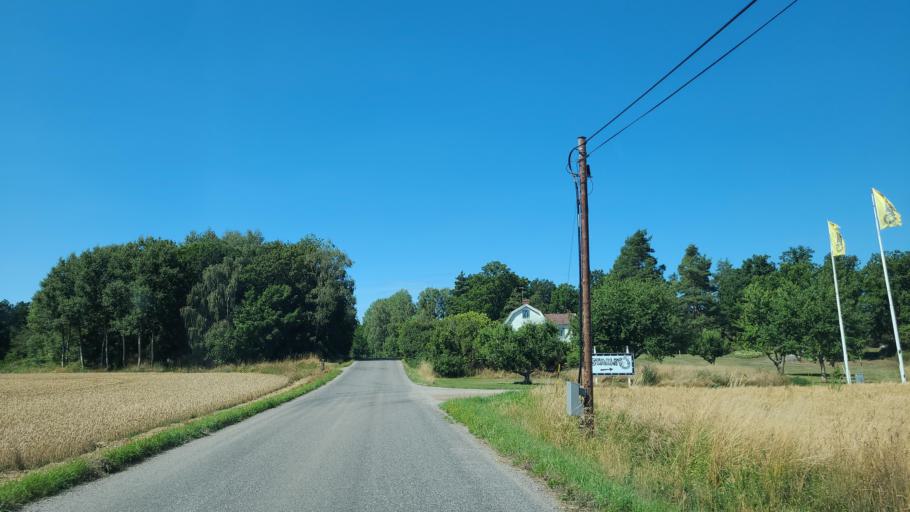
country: SE
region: Kalmar
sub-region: Kalmar Kommun
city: Ljungbyholm
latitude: 56.5757
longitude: 16.0879
